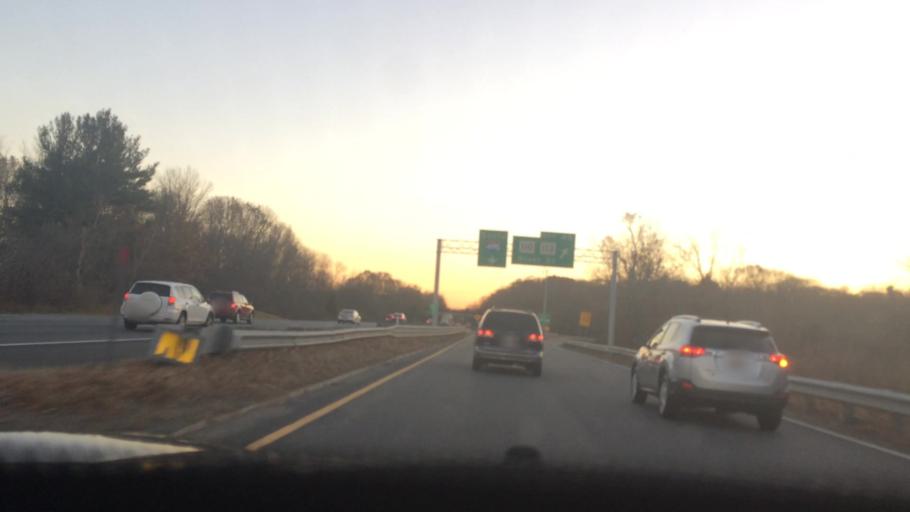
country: US
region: Massachusetts
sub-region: Essex County
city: Haverhill
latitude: 42.7777
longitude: -71.1182
